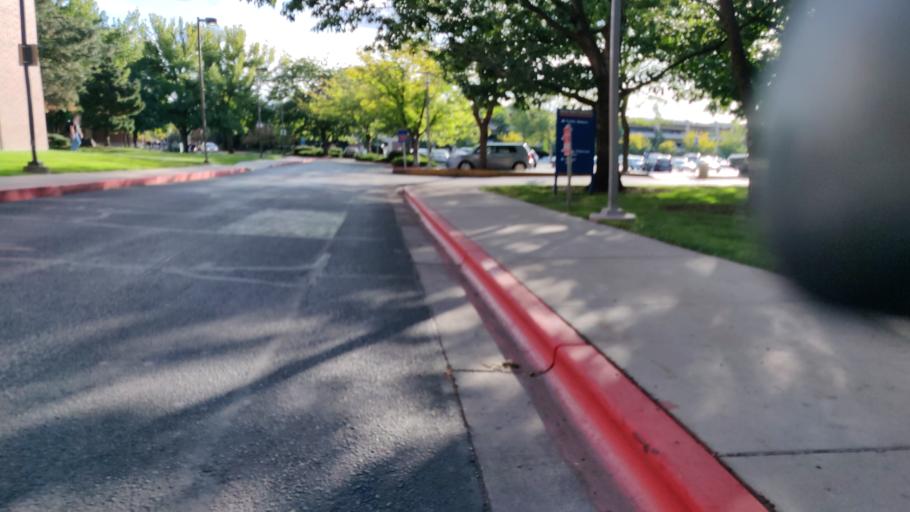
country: US
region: Idaho
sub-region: Ada County
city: Boise
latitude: 43.6063
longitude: -116.2065
